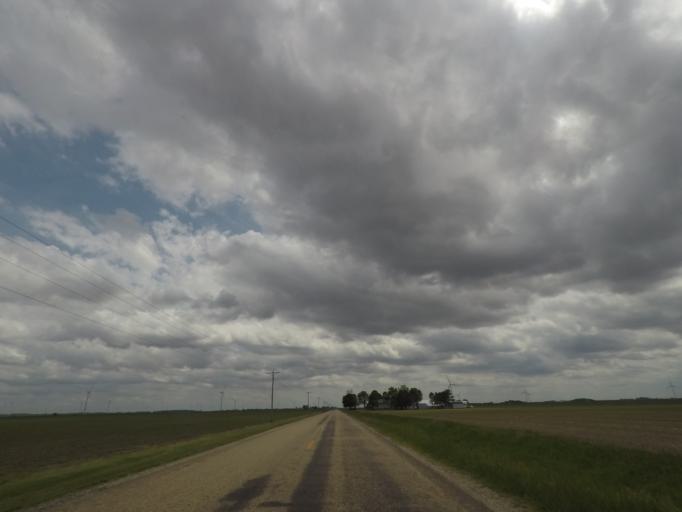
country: US
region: Illinois
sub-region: Macon County
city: Warrensburg
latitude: 40.0614
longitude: -89.0861
